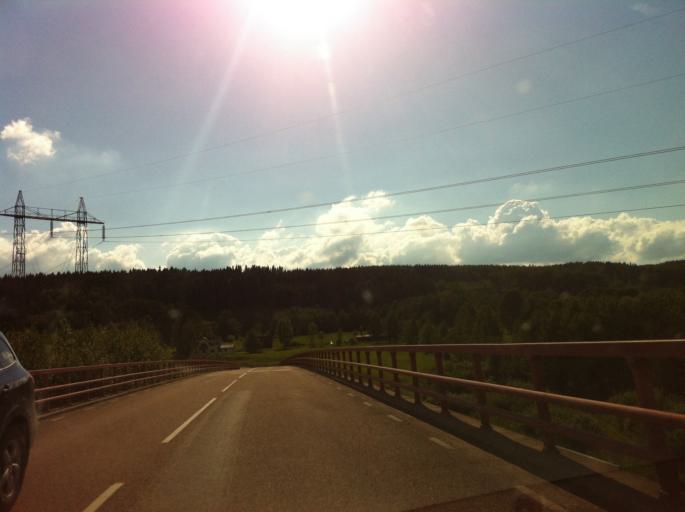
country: SE
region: Vaermland
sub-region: Kils Kommun
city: Kil
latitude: 59.6120
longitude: 13.3121
